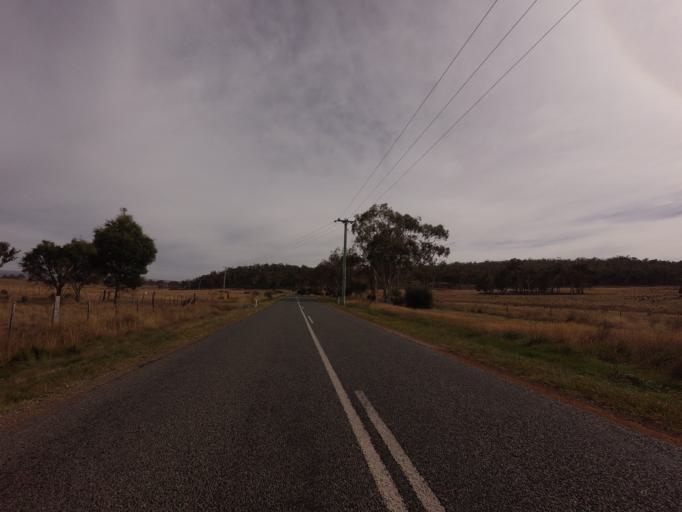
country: AU
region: Tasmania
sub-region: Brighton
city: Bridgewater
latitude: -42.3368
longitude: 147.4020
